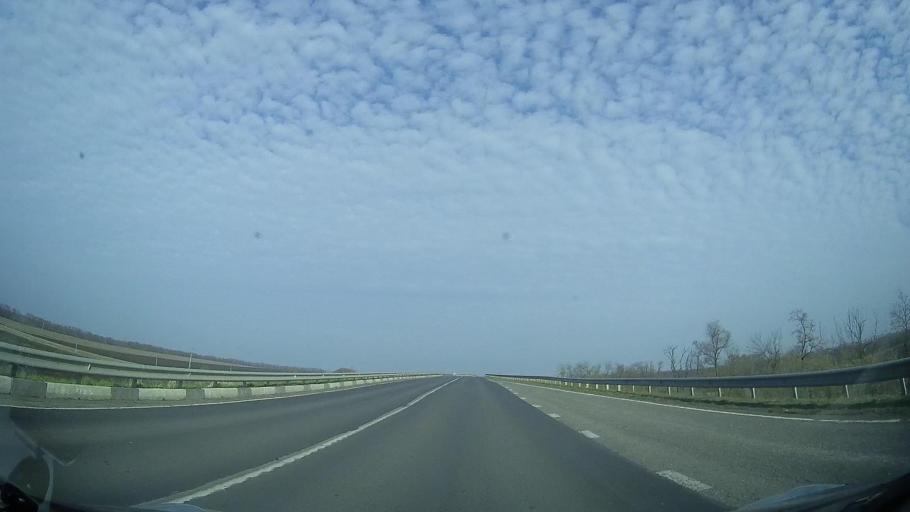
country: RU
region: Rostov
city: Tselina
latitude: 46.5270
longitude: 41.1674
